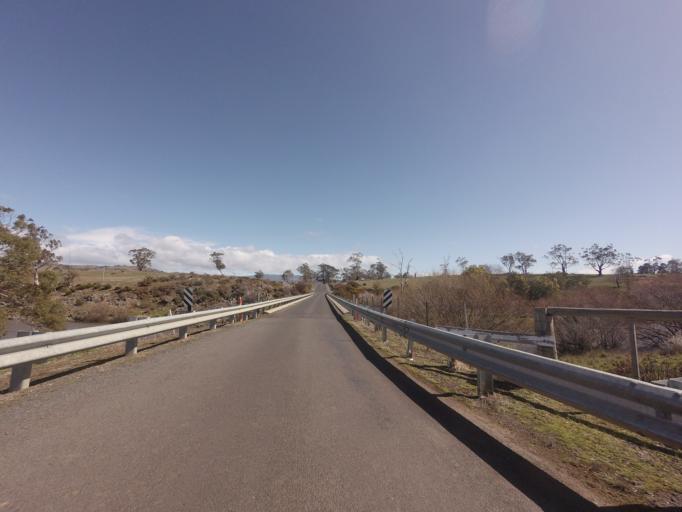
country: AU
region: Tasmania
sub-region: Northern Midlands
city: Evandale
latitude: -41.9076
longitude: 147.3917
